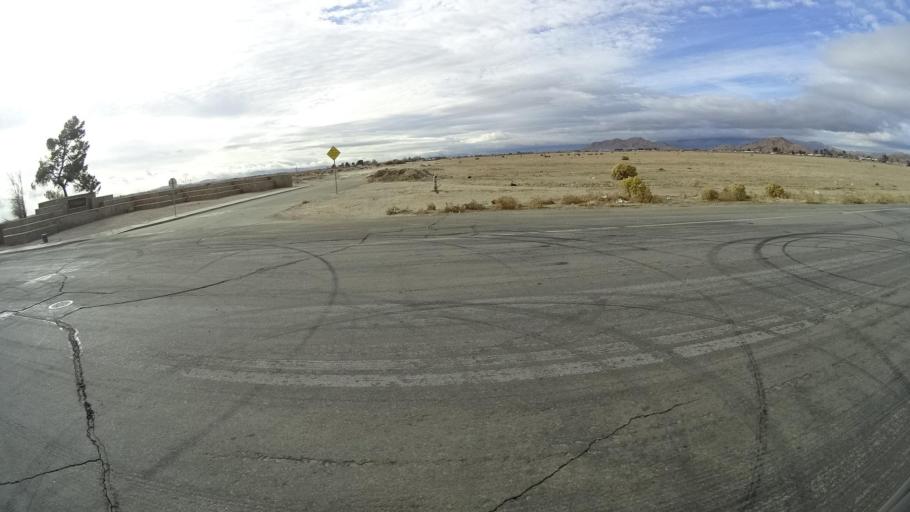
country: US
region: California
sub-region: Kern County
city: Rosamond
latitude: 34.8554
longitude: -118.2016
